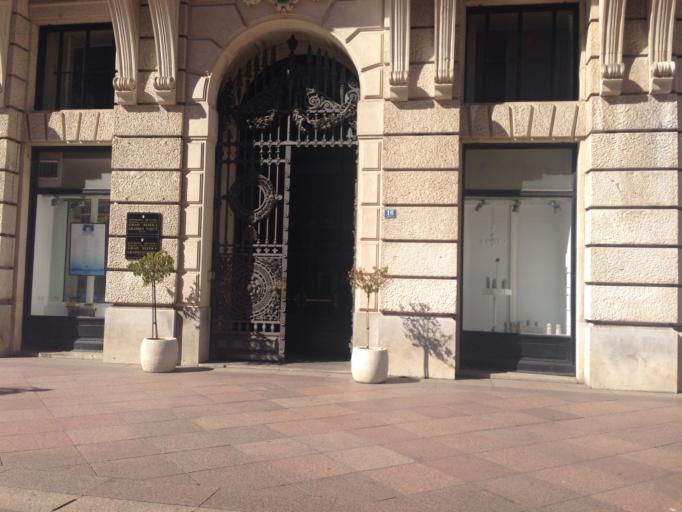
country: HR
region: Primorsko-Goranska
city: Drenova
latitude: 45.3269
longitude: 14.4423
